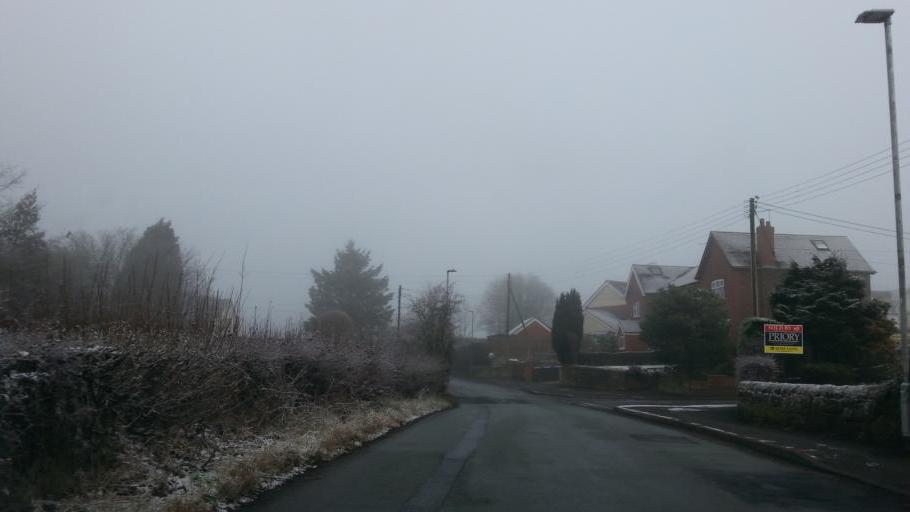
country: GB
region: England
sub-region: Staffordshire
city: Biddulph
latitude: 53.1244
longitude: -2.1802
